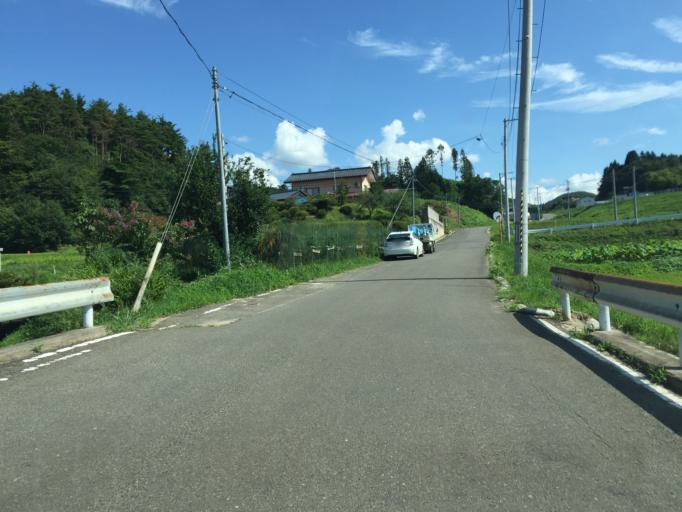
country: JP
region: Fukushima
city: Fukushima-shi
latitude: 37.7007
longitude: 140.5220
